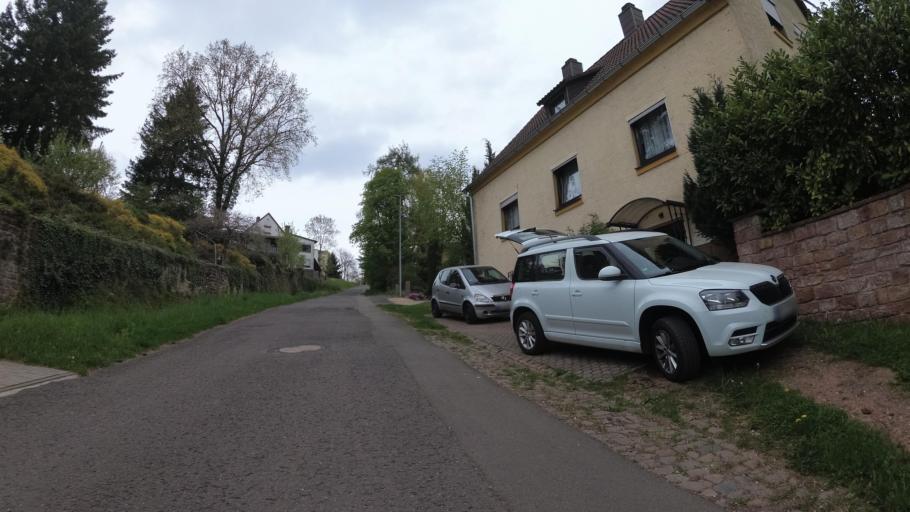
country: DE
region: Rheinland-Pfalz
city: Zweibrucken
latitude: 49.2551
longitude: 7.3603
